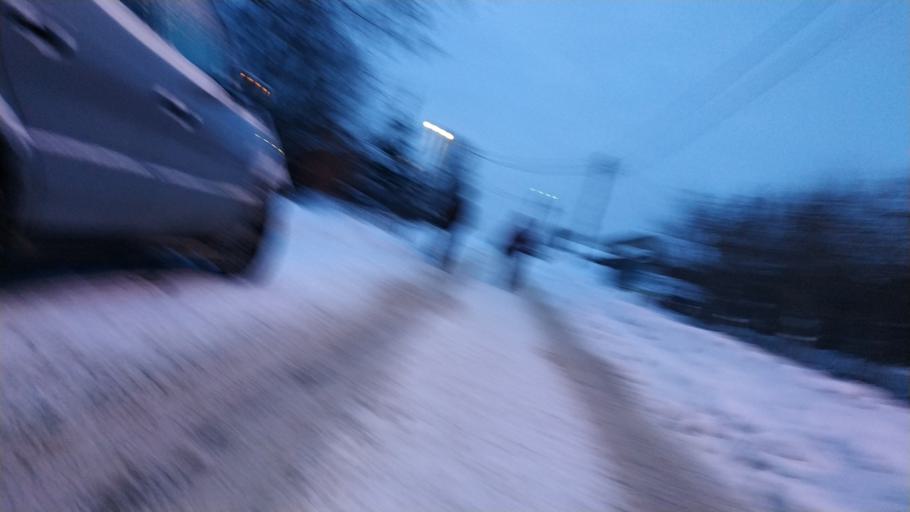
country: RU
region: Moskovskaya
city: Nemchinovka
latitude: 55.7345
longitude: 37.3523
